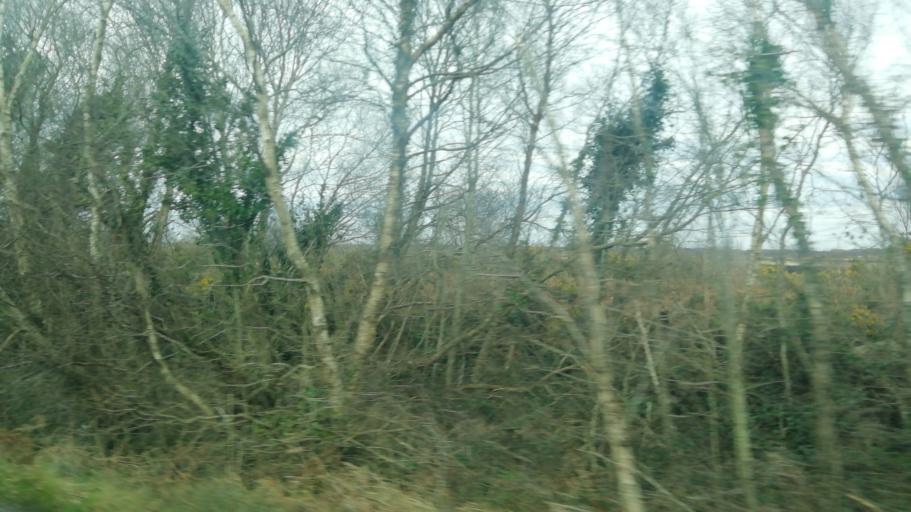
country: IE
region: Leinster
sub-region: Kildare
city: Rathangan
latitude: 53.2583
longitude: -7.0148
